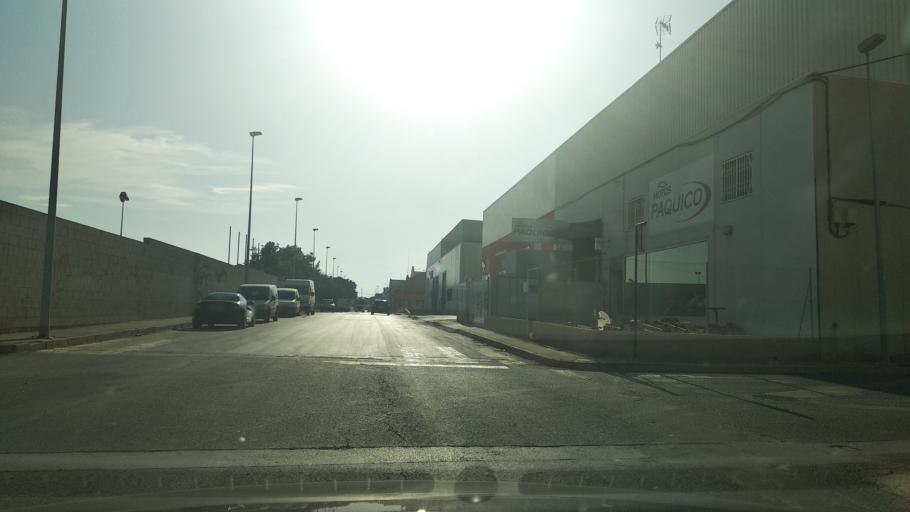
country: ES
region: Murcia
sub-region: Murcia
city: San Javier
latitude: 37.8095
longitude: -0.8401
